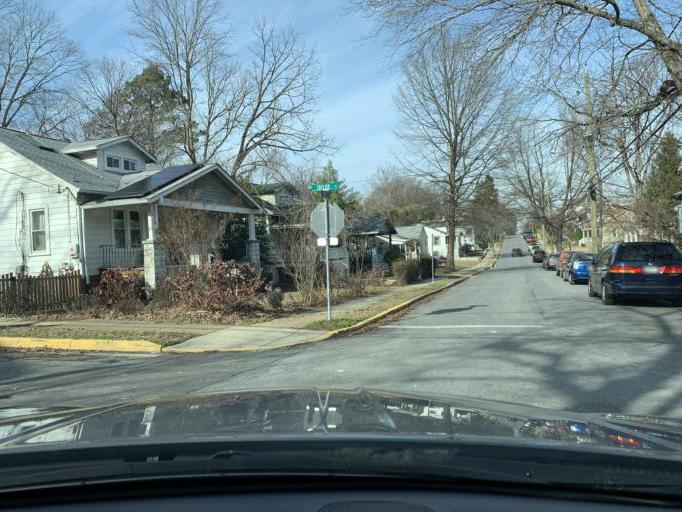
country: US
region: Maryland
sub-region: Prince George's County
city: Mount Rainier
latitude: 38.9412
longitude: -76.9648
